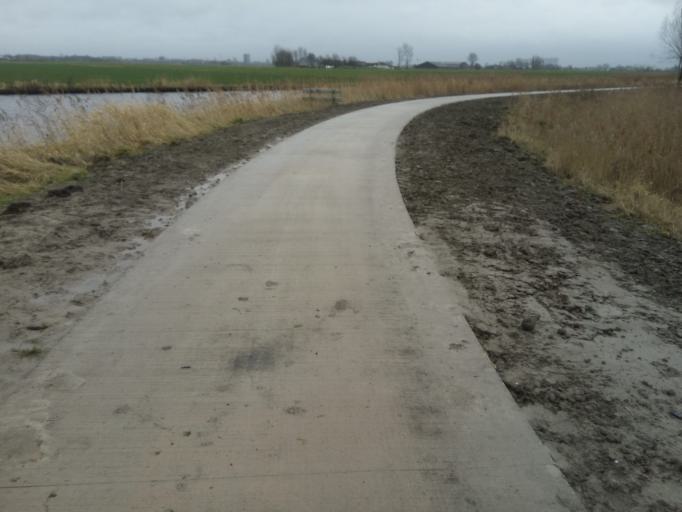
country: NL
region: Groningen
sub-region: Gemeente Zuidhorn
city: Aduard
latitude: 53.2595
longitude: 6.4818
